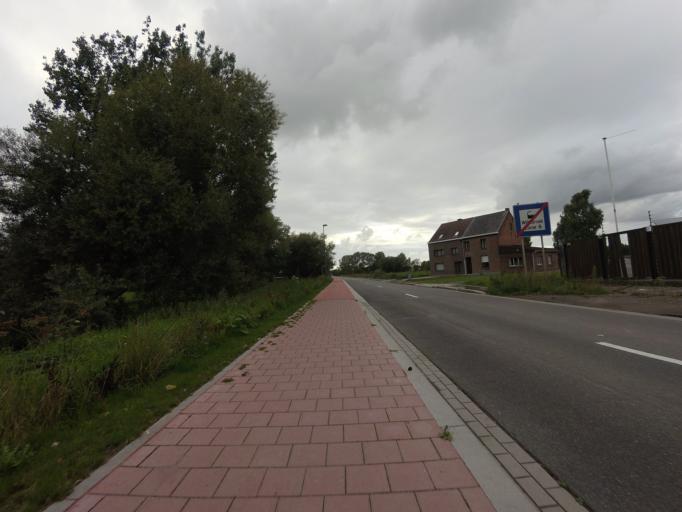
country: BE
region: Flanders
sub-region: Provincie Antwerpen
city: Willebroek
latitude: 51.0405
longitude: 4.3450
